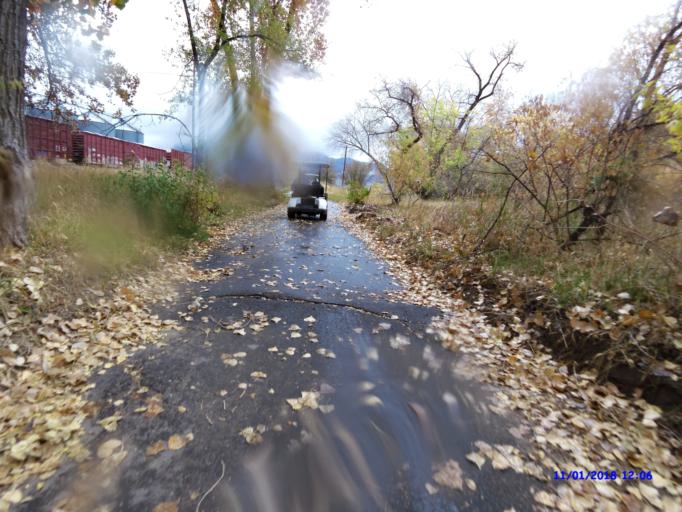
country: US
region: Utah
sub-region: Weber County
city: Ogden
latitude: 41.2292
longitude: -111.9928
